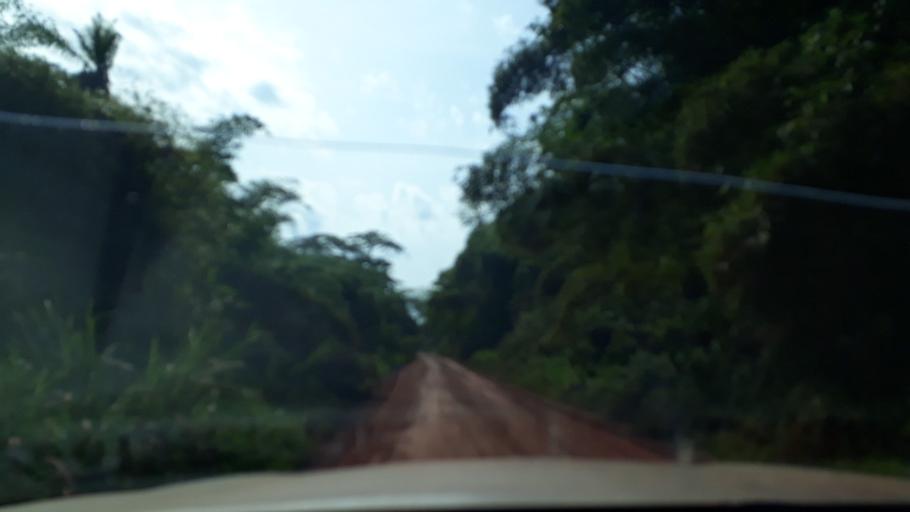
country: CD
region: Eastern Province
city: Wamba
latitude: 1.4048
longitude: 27.8329
